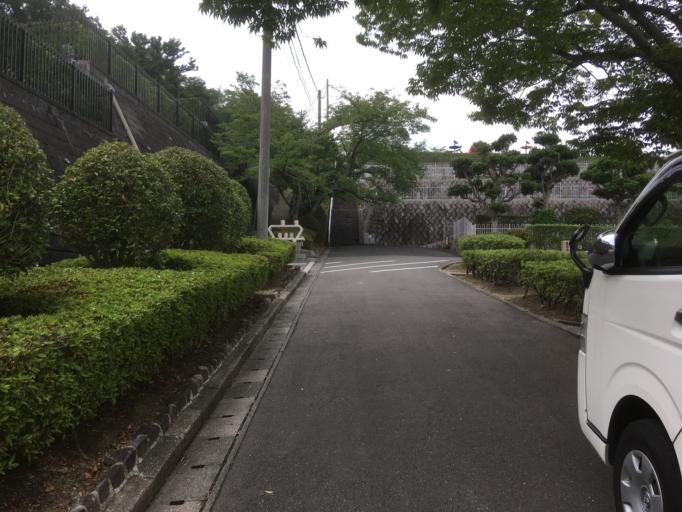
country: JP
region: Nara
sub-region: Ikoma-shi
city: Ikoma
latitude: 34.7386
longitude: 135.6898
